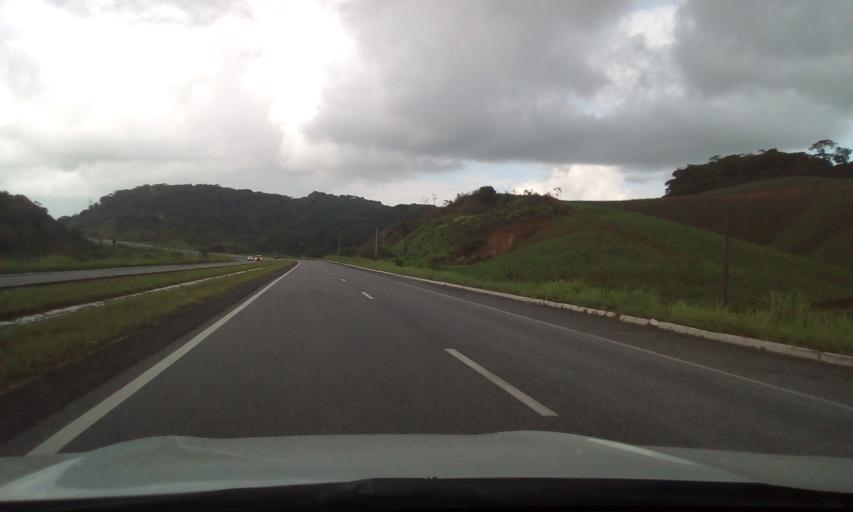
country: BR
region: Pernambuco
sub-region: Cabo De Santo Agostinho
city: Cabo
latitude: -8.2577
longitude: -35.0420
